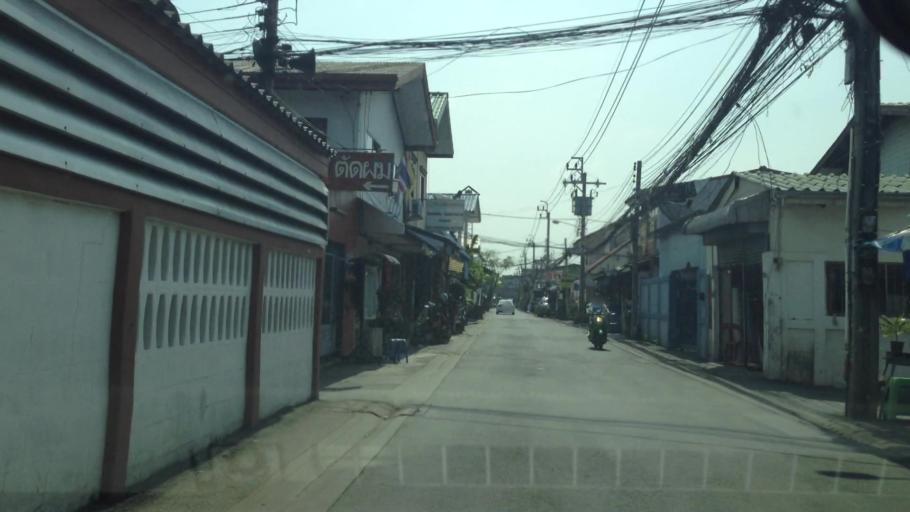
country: TH
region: Bangkok
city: Sai Mai
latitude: 13.9025
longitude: 100.6302
